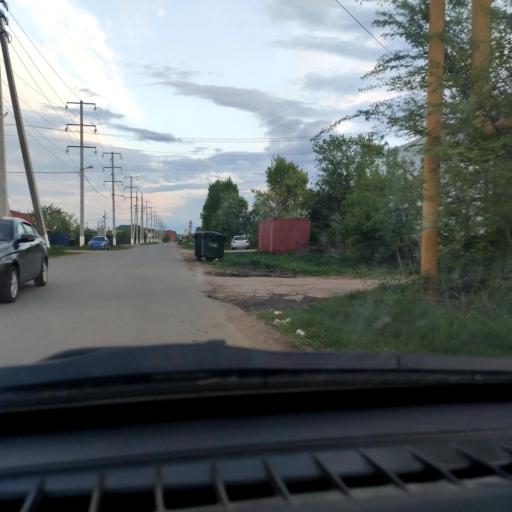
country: RU
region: Samara
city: Podstepki
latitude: 53.5197
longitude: 49.1128
